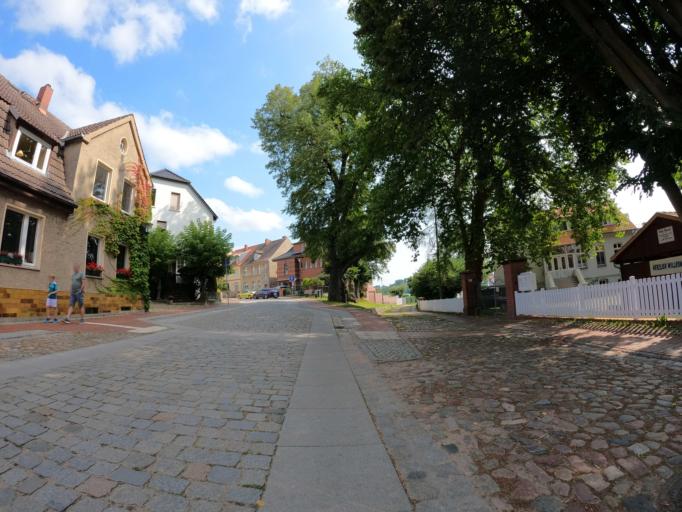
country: DE
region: Mecklenburg-Vorpommern
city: Malchow
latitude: 53.4786
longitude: 12.4286
